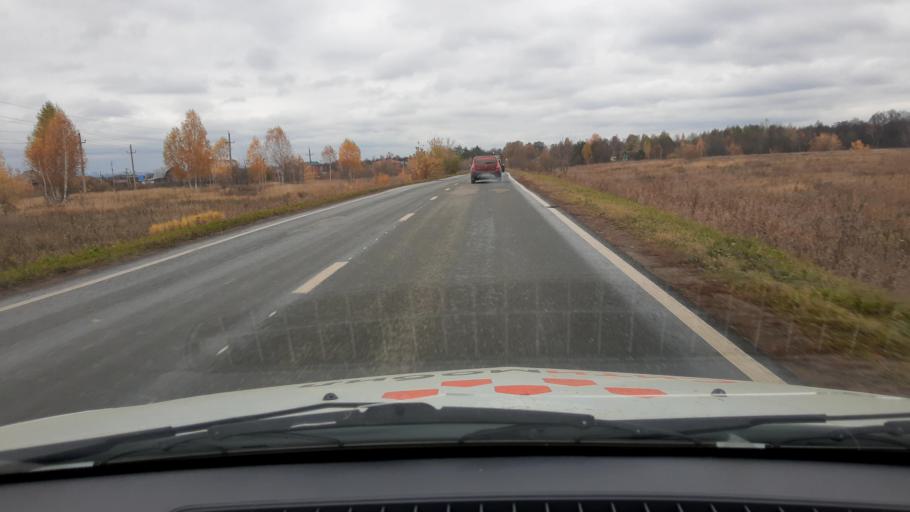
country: RU
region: Bashkortostan
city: Iglino
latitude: 54.7449
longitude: 56.2155
